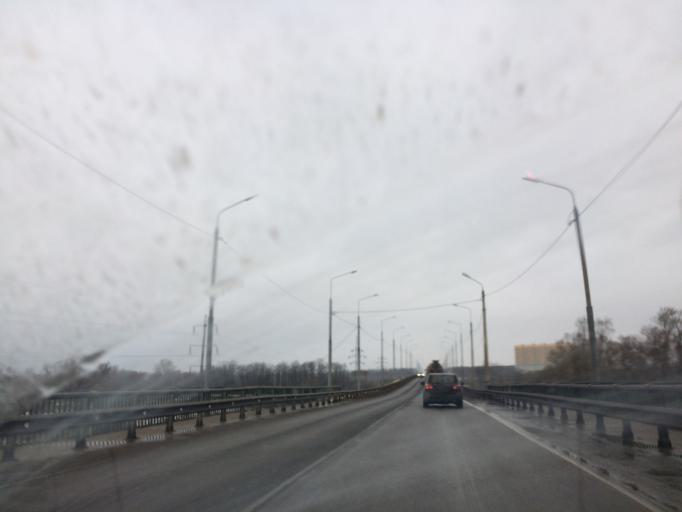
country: RU
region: Tula
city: Mendeleyevskiy
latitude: 54.1576
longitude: 37.5639
